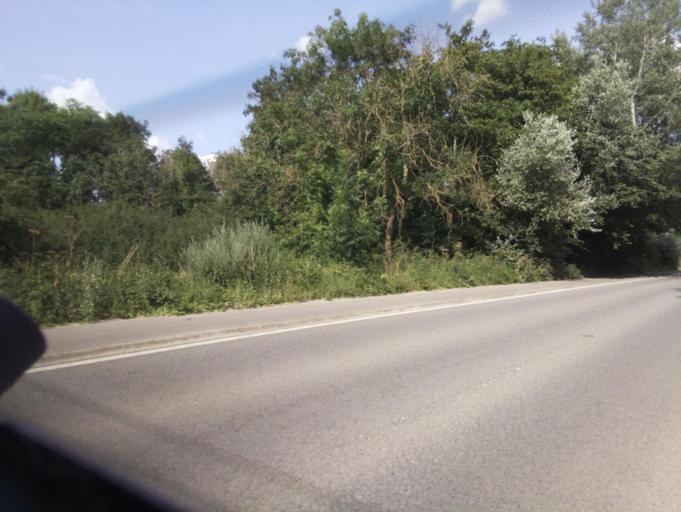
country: GB
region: England
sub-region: Wiltshire
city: Minety
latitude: 51.6560
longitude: -1.9270
